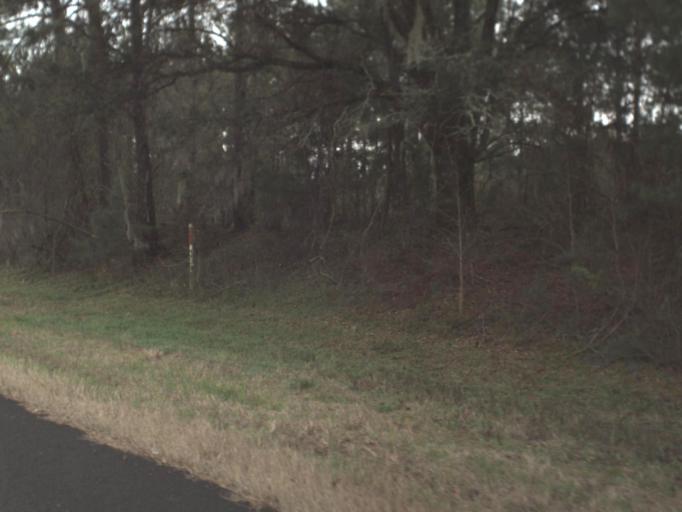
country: US
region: Florida
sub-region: Jefferson County
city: Monticello
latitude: 30.3996
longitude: -83.8801
